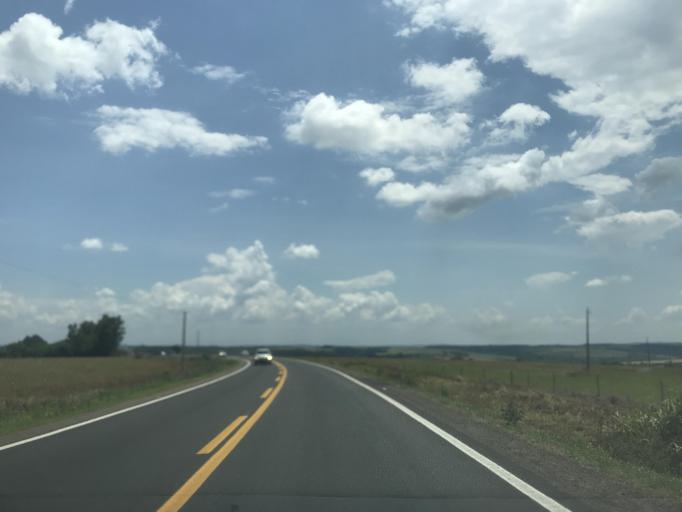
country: BR
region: Goias
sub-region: Bela Vista De Goias
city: Bela Vista de Goias
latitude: -17.1040
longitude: -48.6640
